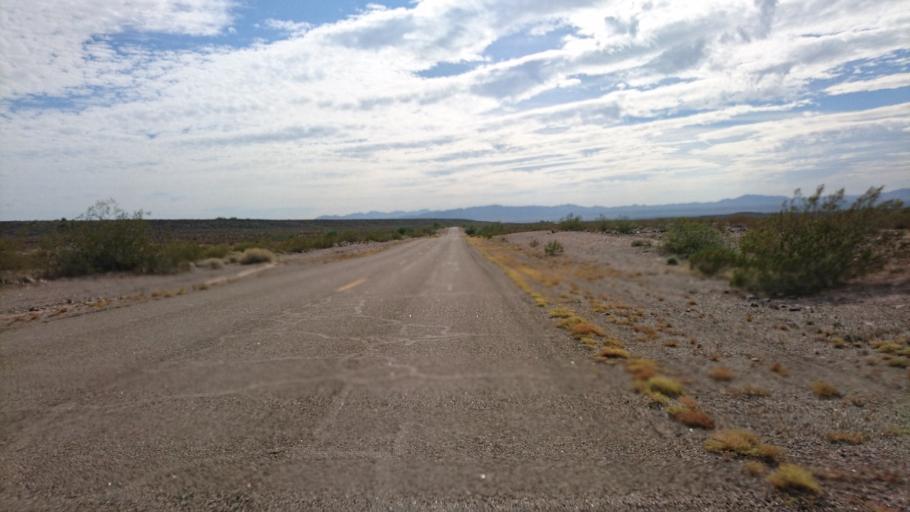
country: US
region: Arizona
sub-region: Mohave County
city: Mohave Valley
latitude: 34.8642
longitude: -114.4428
